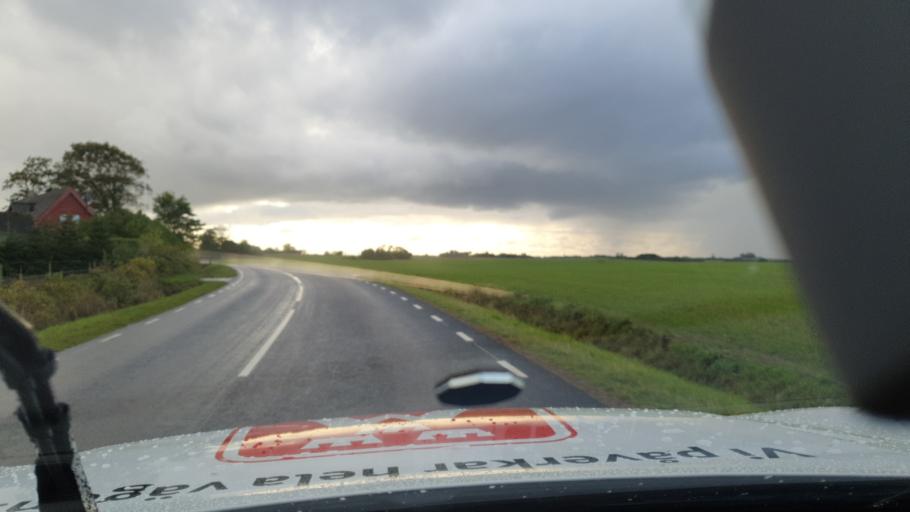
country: SE
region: Skane
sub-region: Trelleborgs Kommun
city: Anderslov
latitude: 55.4330
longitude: 13.3094
